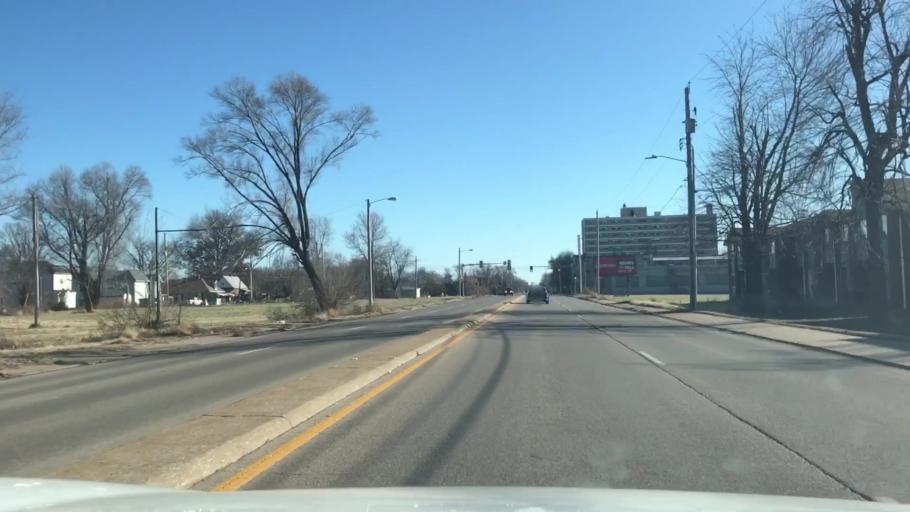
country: US
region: Illinois
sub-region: Saint Clair County
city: East Saint Louis
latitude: 38.6201
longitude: -90.1518
